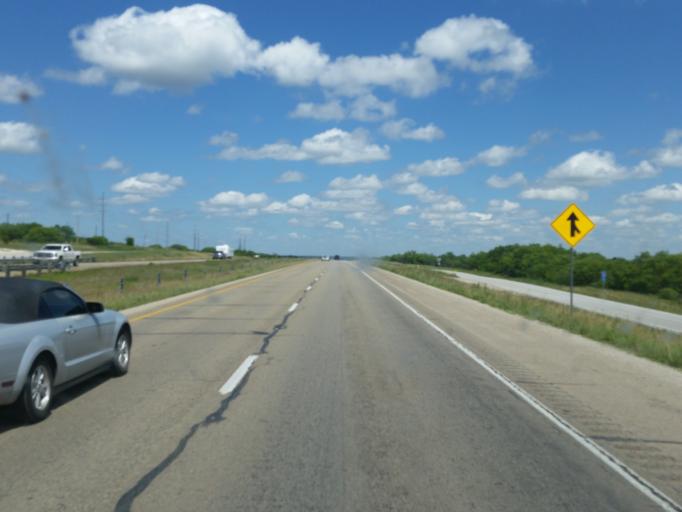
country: US
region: Texas
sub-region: Callahan County
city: Baird
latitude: 32.3914
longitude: -99.3447
